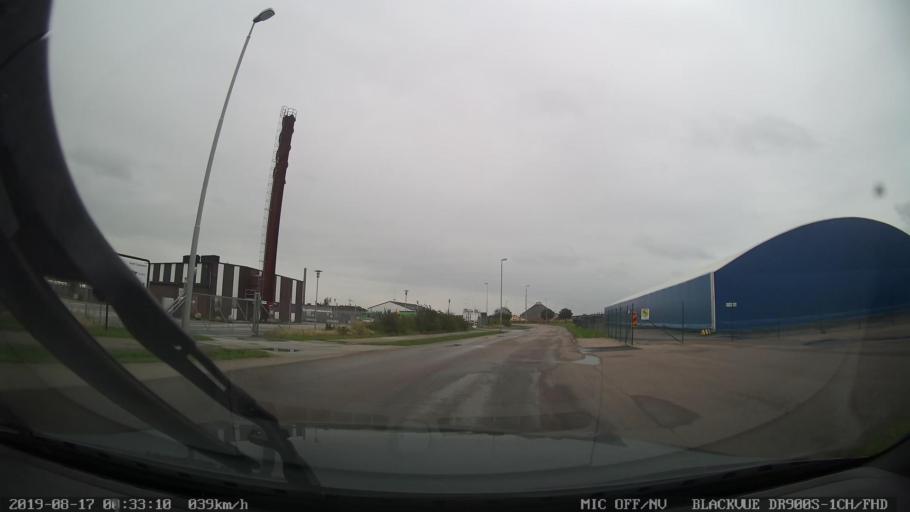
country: SE
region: Skane
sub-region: Landskrona
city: Landskrona
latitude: 55.8644
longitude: 12.8344
